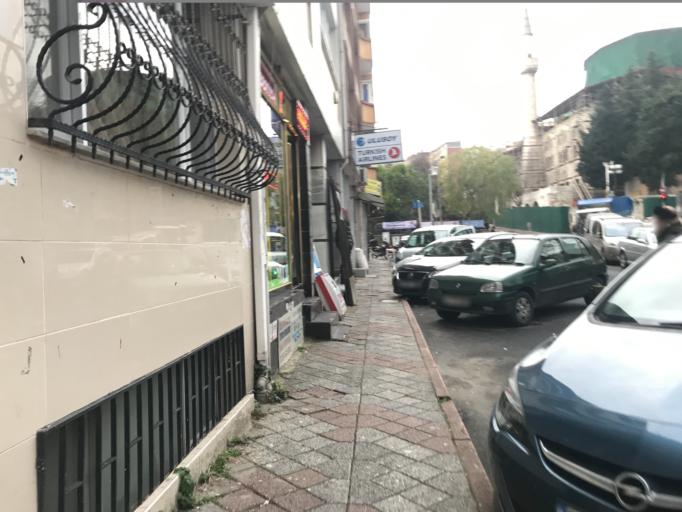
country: TR
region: Istanbul
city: Istanbul
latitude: 41.0208
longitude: 28.9440
